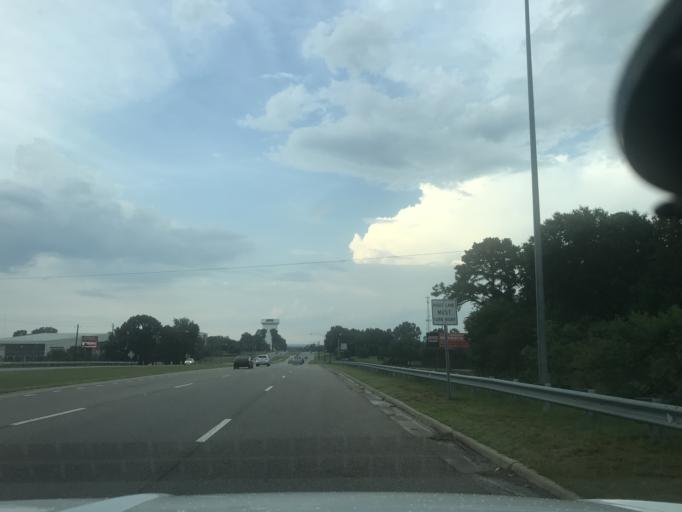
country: US
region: Alabama
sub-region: Montgomery County
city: Pike Road
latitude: 32.3637
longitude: -86.1711
